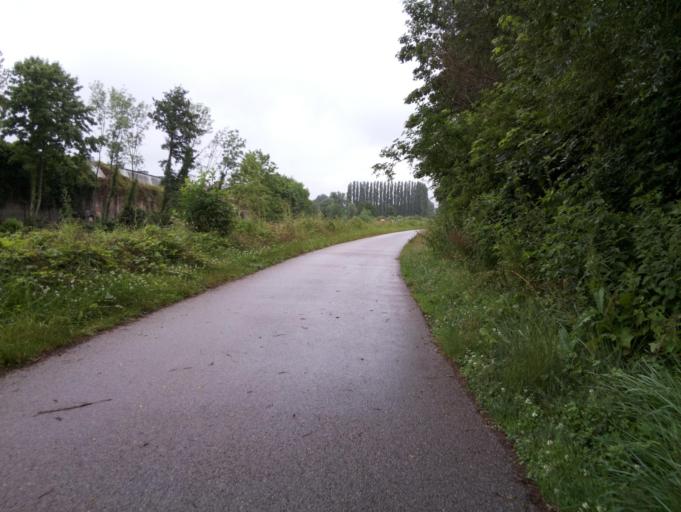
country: FR
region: Picardie
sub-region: Departement de la Somme
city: Ailly-sur-Somme
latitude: 49.9279
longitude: 2.2057
